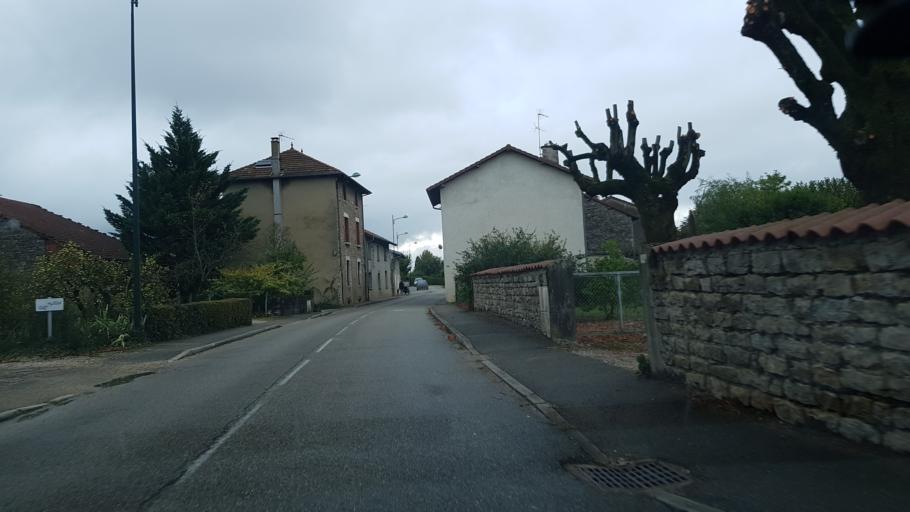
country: FR
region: Rhone-Alpes
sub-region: Departement de l'Ain
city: Tossiat
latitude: 46.1380
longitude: 5.3170
